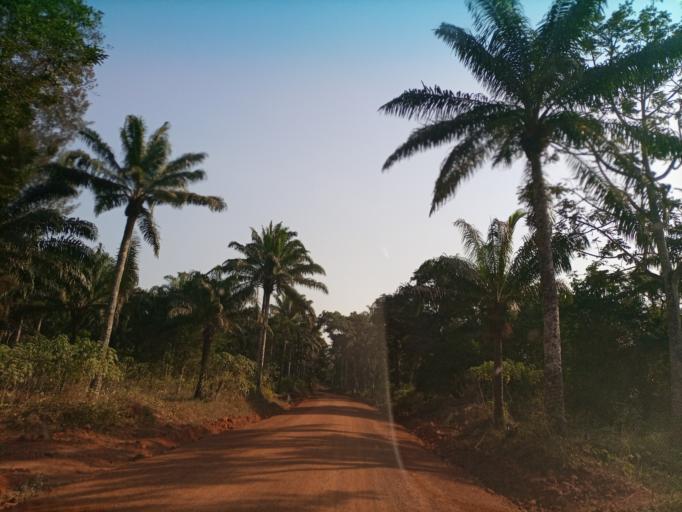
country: NG
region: Enugu
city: Opi
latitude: 6.7748
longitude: 7.3903
